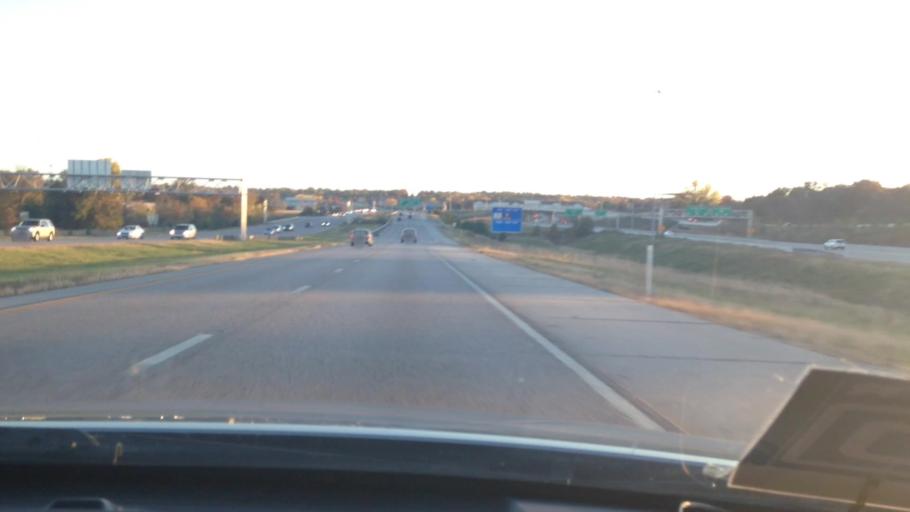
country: US
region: Kansas
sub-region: Johnson County
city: Lenexa
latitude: 38.9330
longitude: -94.7051
